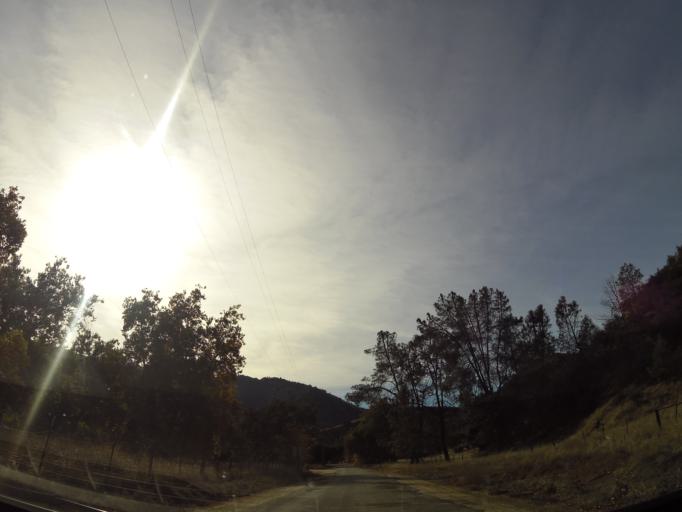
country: US
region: California
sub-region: San Benito County
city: Ridgemark
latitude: 36.6932
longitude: -121.3385
